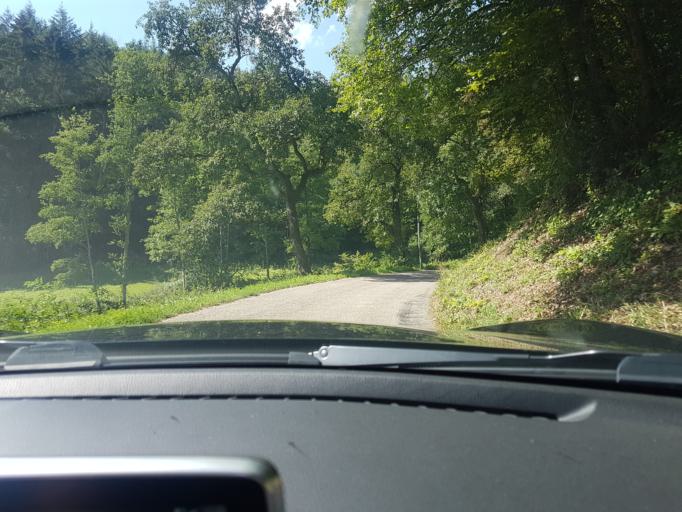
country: DE
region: Baden-Wuerttemberg
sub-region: Regierungsbezirk Stuttgart
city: Mockmuhl
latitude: 49.3273
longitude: 9.3887
